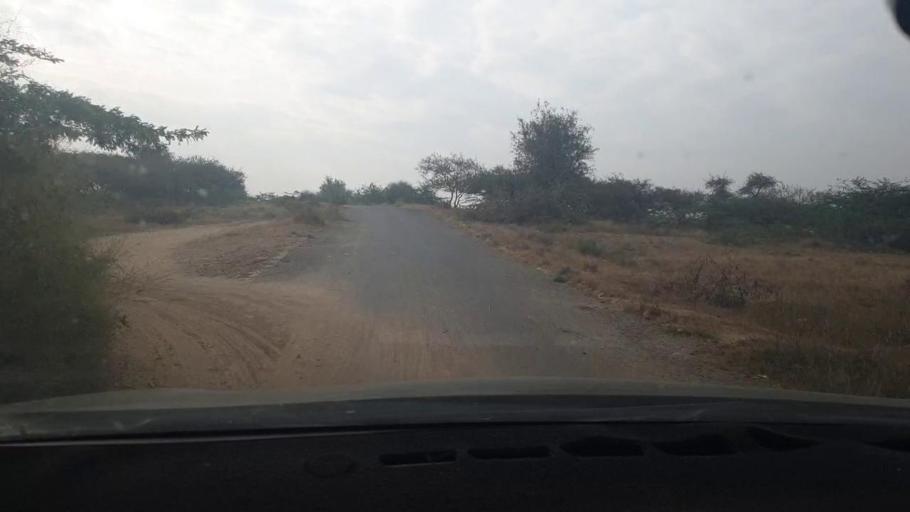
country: PK
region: Sindh
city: Malir Cantonment
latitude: 24.9568
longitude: 67.4077
